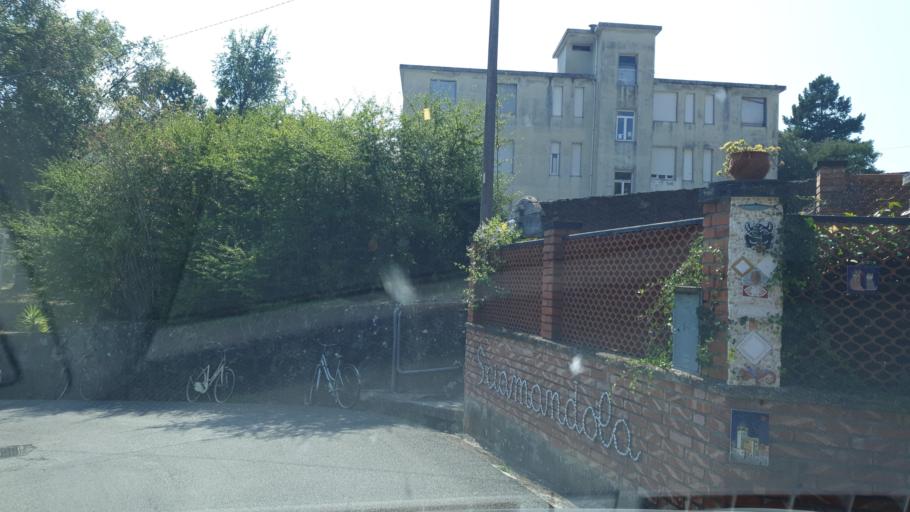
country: IT
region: Liguria
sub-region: Provincia di La Spezia
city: Levanto
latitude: 44.1772
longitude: 9.6199
